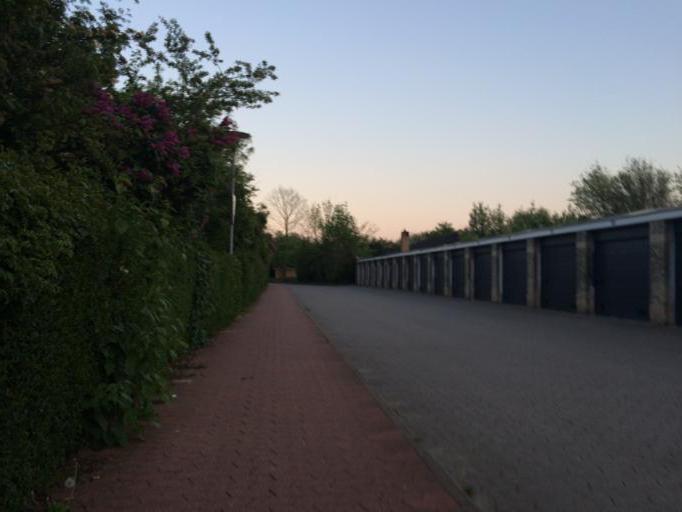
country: DK
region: Capital Region
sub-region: Tarnby Kommune
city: Tarnby
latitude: 55.6378
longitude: 12.6295
